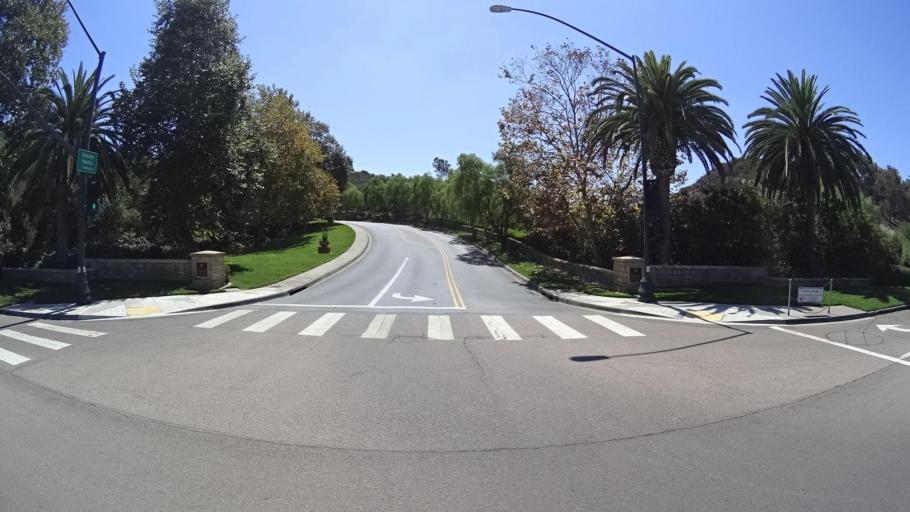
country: US
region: California
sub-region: San Diego County
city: Fairbanks Ranch
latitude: 32.9754
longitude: -117.2233
